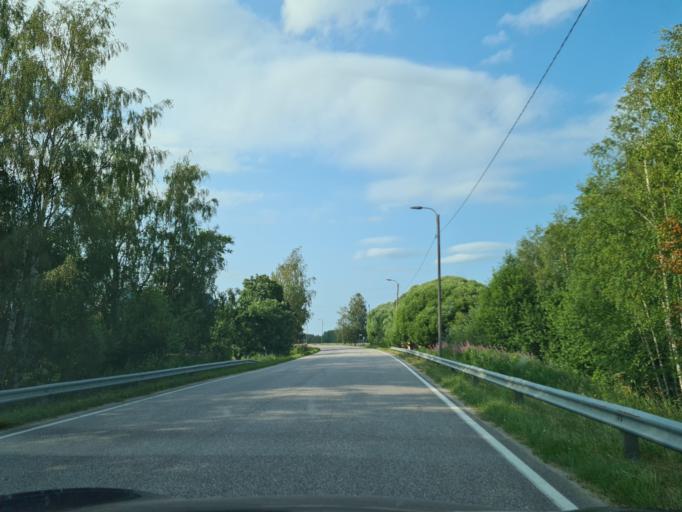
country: FI
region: Ostrobothnia
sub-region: Vaasa
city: Vaehaekyroe
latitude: 63.0089
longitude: 22.1492
